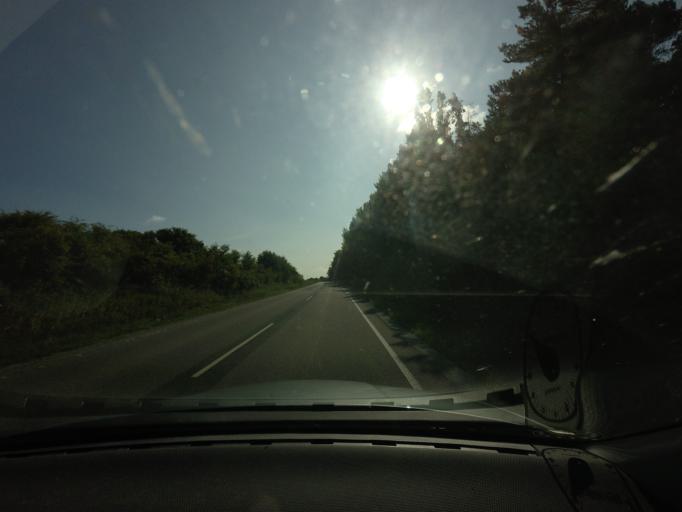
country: DK
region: Zealand
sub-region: Vordingborg Kommune
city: Praesto
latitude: 55.0103
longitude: 12.1282
